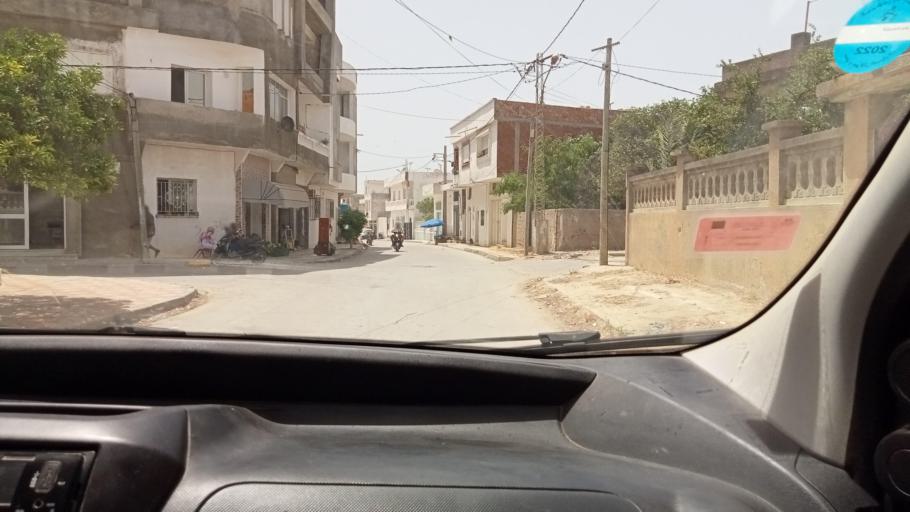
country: TN
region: Nabul
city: Qulaybiyah
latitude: 36.8545
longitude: 11.0884
